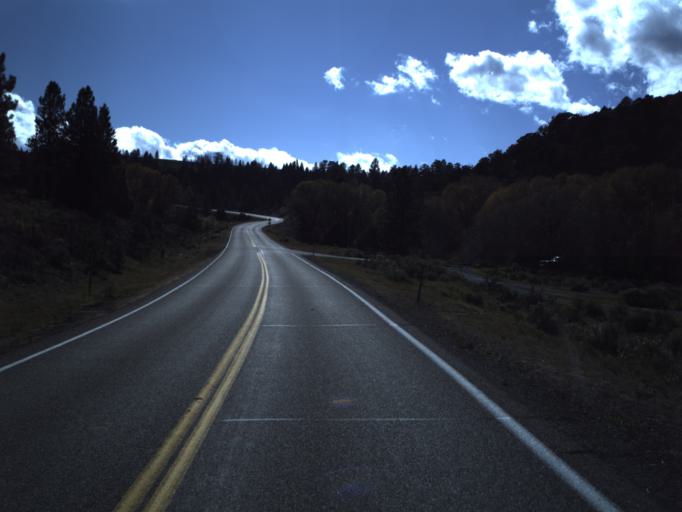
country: US
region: Utah
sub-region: Garfield County
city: Panguitch
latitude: 37.7460
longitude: -112.5864
